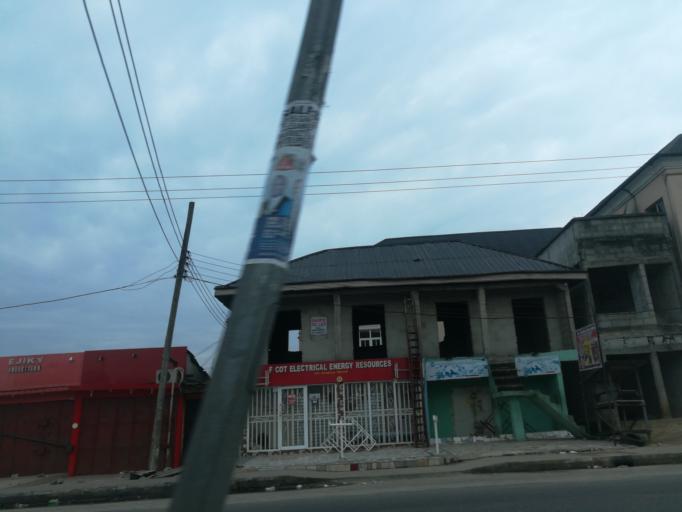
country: NG
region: Rivers
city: Port Harcourt
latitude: 4.8300
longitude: 6.9792
